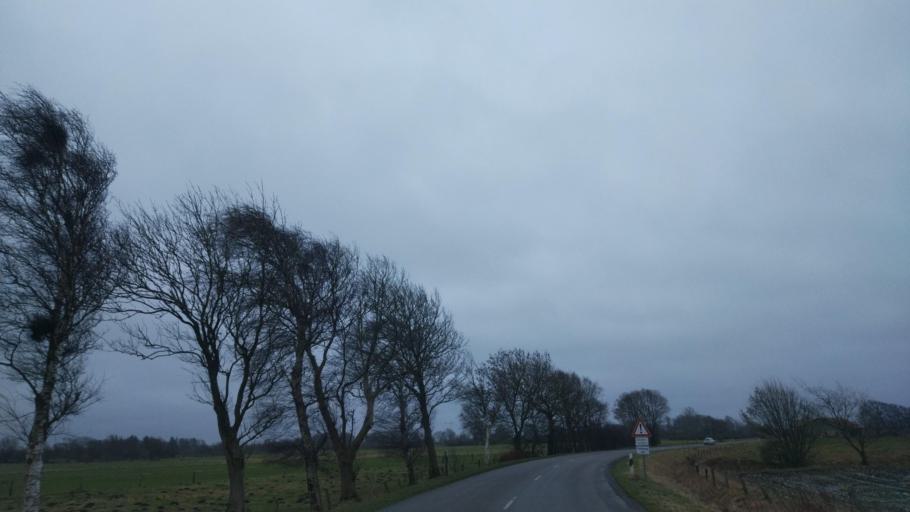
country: DE
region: Schleswig-Holstein
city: Treia
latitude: 54.4929
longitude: 9.3451
